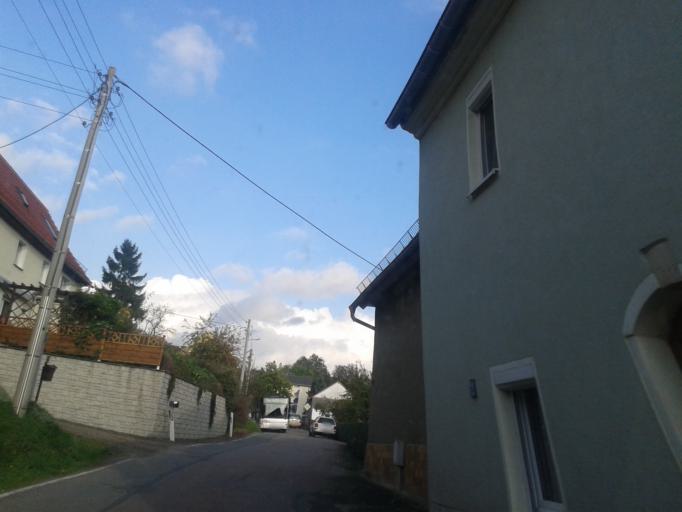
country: DE
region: Saxony
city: Niederschona
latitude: 51.0395
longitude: 13.4382
